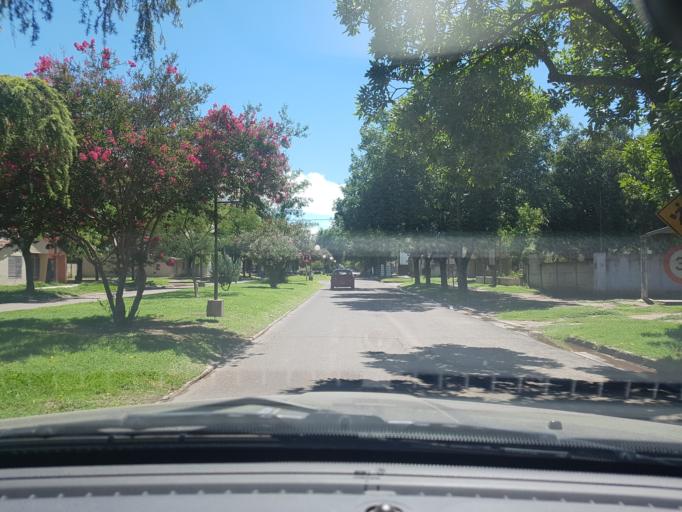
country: AR
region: Cordoba
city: Las Perdices
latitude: -32.7580
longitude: -63.7841
